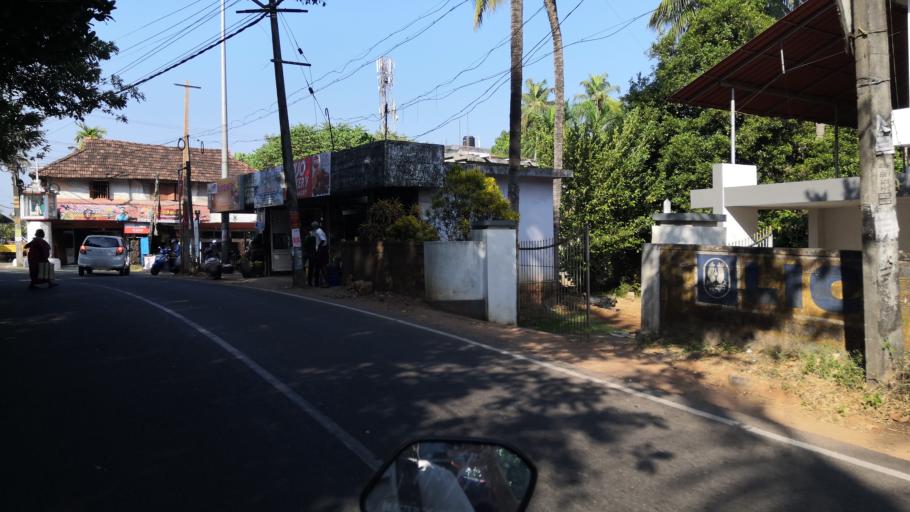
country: IN
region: Kerala
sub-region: Thrissur District
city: Kodungallur
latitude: 10.2399
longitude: 76.2790
